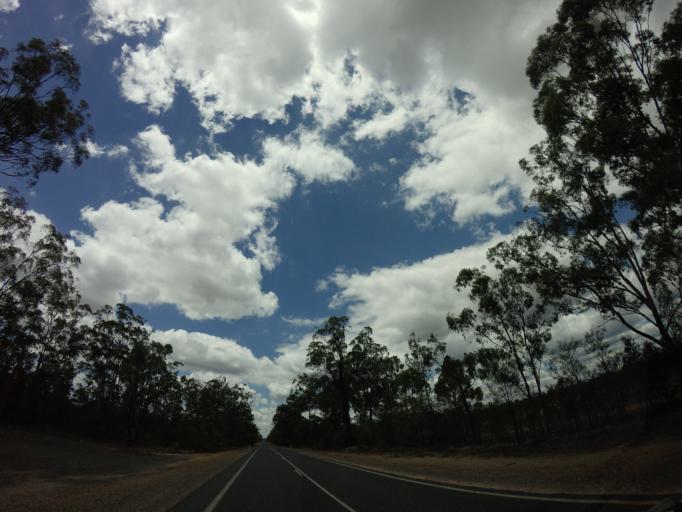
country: AU
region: Queensland
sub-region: Goondiwindi
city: Goondiwindi
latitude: -28.0202
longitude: 150.8547
